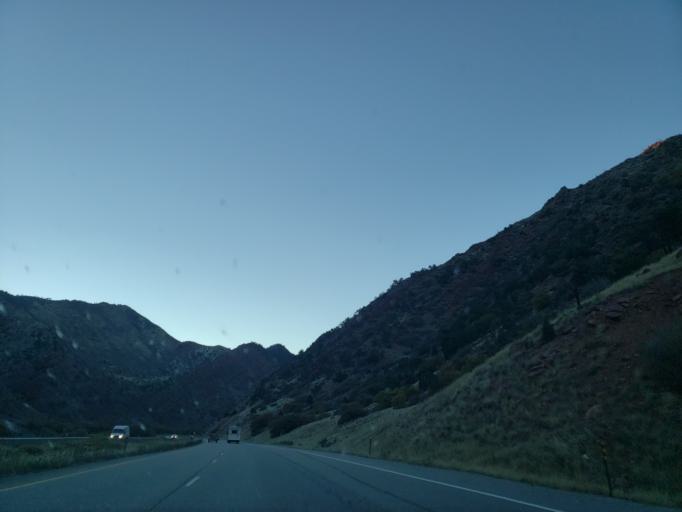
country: US
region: Colorado
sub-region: Garfield County
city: Glenwood Springs
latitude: 39.5656
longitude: -107.4160
